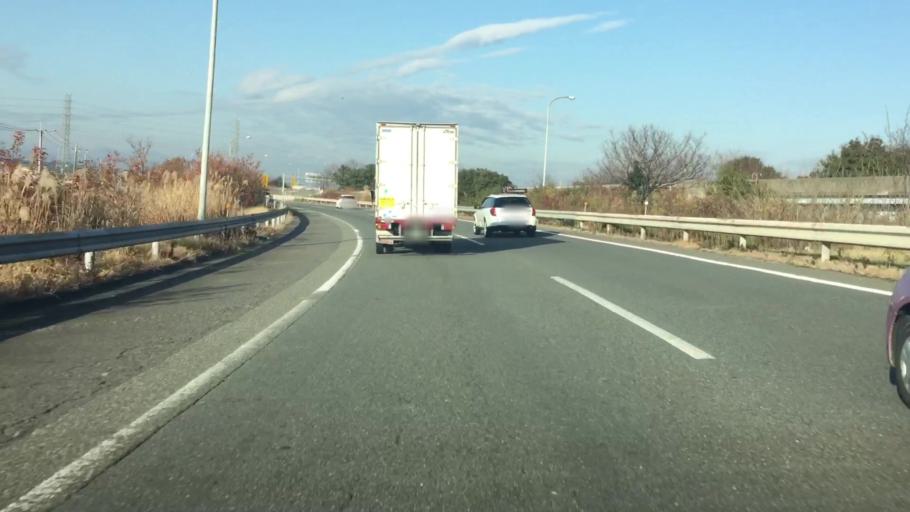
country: JP
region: Gunma
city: Fujioka
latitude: 36.2725
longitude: 139.0938
